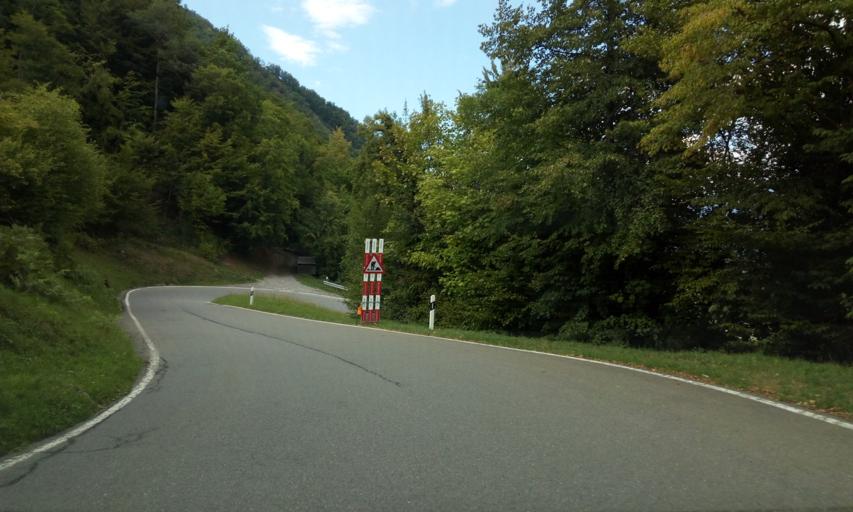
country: CH
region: Valais
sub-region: Monthey District
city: Vionnaz
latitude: 46.3094
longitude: 6.8922
